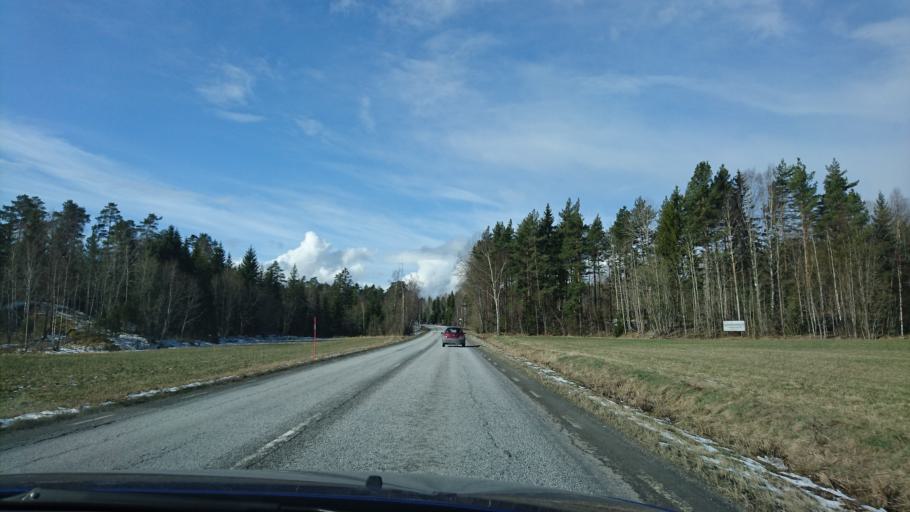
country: SE
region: Stockholm
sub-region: Norrtalje Kommun
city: Norrtalje
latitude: 59.7762
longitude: 18.7564
